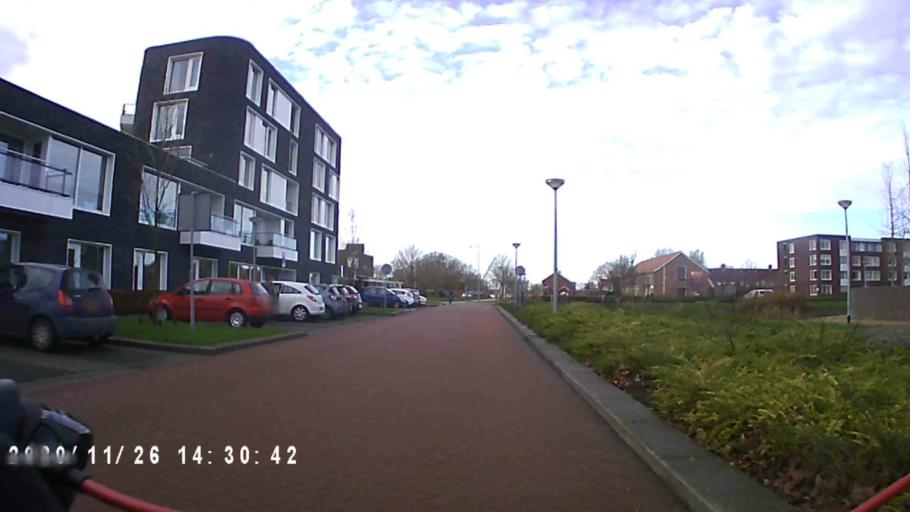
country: NL
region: Groningen
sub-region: Gemeente Appingedam
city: Appingedam
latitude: 53.3156
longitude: 6.8640
